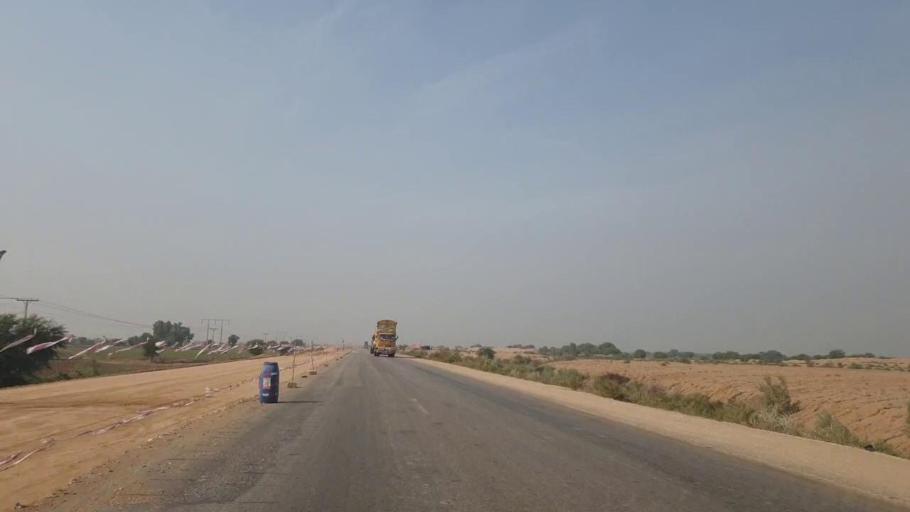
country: PK
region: Sindh
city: Sann
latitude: 26.1382
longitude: 68.0413
